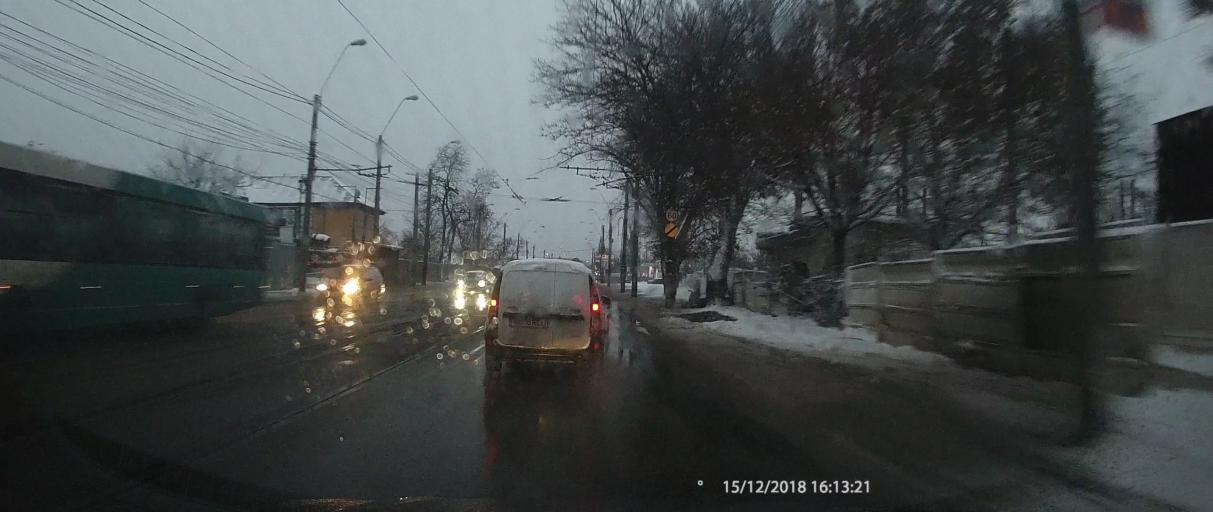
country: RO
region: Galati
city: Galati
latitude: 45.4639
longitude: 28.0335
